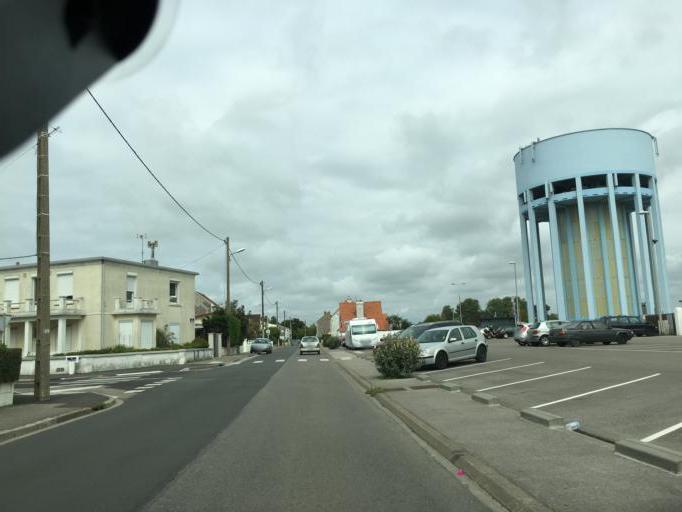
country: FR
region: Nord-Pas-de-Calais
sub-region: Departement du Pas-de-Calais
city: Berck-Plage
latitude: 50.4019
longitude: 1.5699
